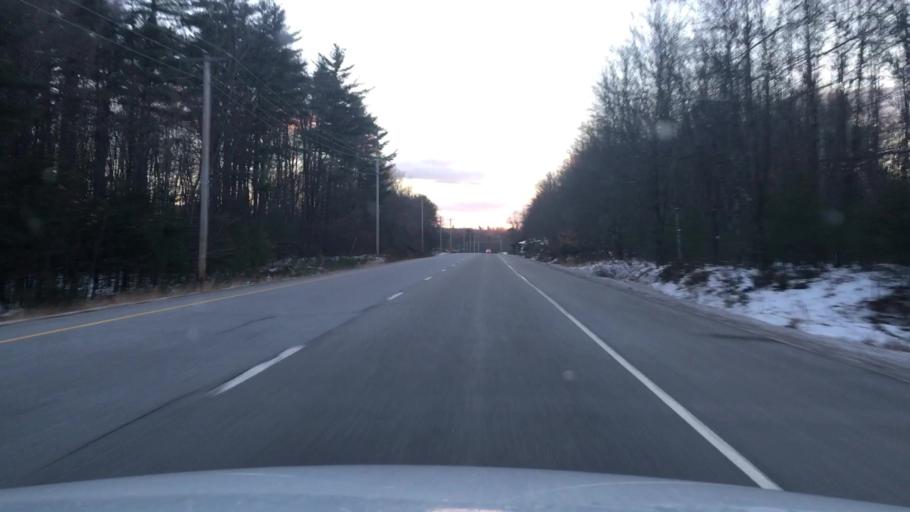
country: US
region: Maine
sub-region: Androscoggin County
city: Auburn
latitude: 44.0533
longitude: -70.2562
